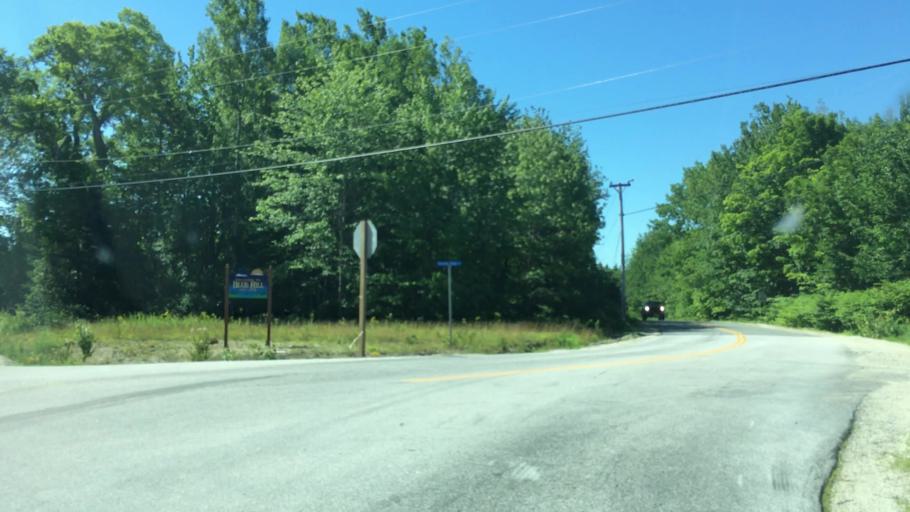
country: US
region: Maine
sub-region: Hancock County
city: Penobscot
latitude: 44.4631
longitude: -68.6371
